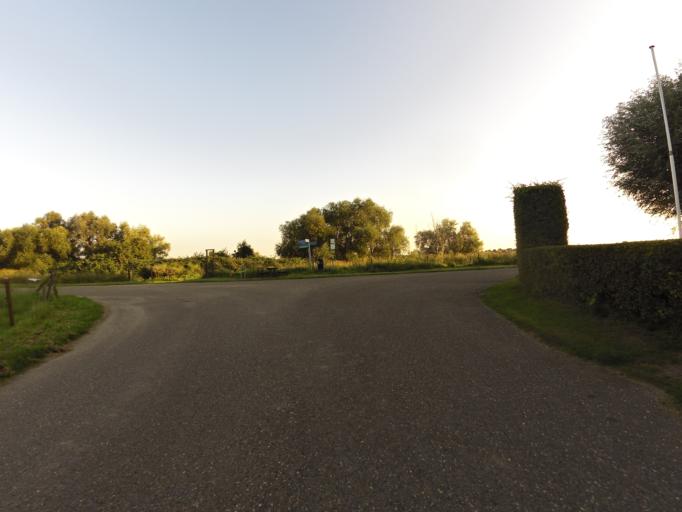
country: NL
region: Gelderland
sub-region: Gemeente Zevenaar
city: Zevenaar
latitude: 51.8744
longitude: 6.0508
